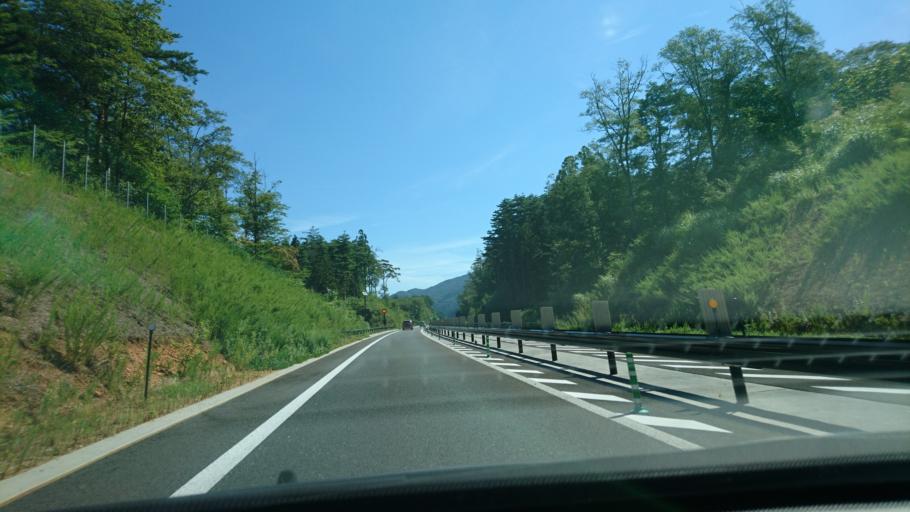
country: JP
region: Iwate
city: Tono
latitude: 39.2986
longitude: 141.4148
